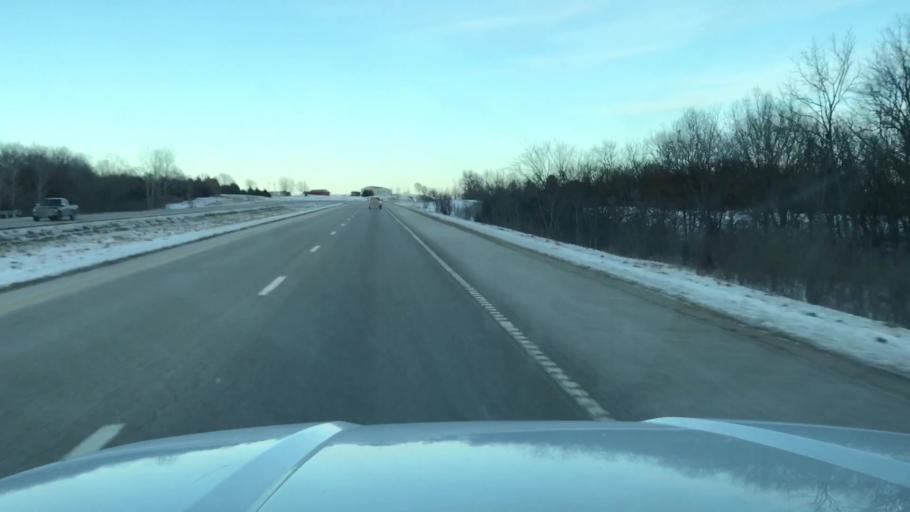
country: US
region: Missouri
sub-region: Clinton County
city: Gower
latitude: 39.7592
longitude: -94.5732
